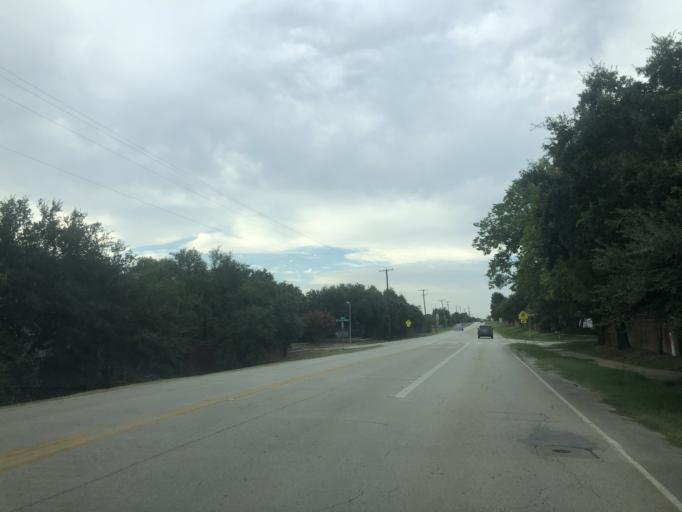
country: US
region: Texas
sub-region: Tarrant County
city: Southlake
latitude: 32.9500
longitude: -97.1511
